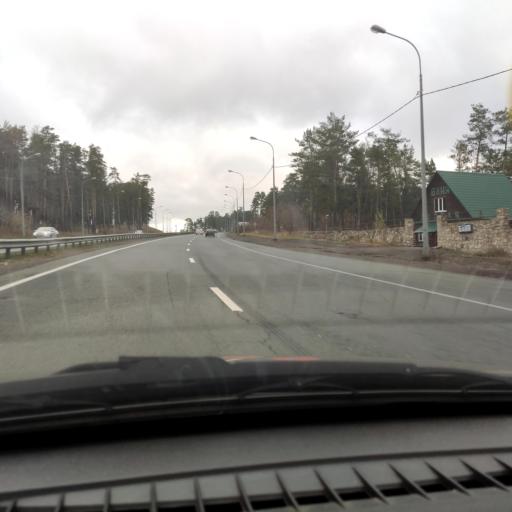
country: RU
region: Samara
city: Zhigulevsk
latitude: 53.5348
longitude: 49.5165
